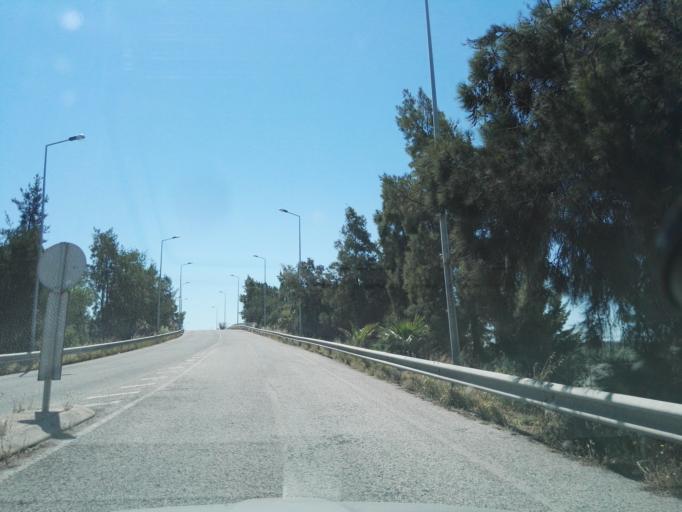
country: PT
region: Lisbon
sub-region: Vila Franca de Xira
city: Sobralinho
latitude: 38.8869
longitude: -9.0394
